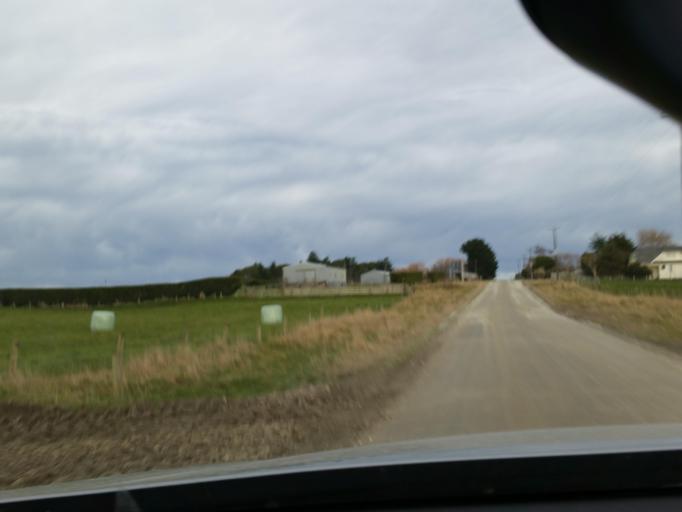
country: NZ
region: Southland
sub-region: Invercargill City
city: Invercargill
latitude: -46.4146
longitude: 168.5061
